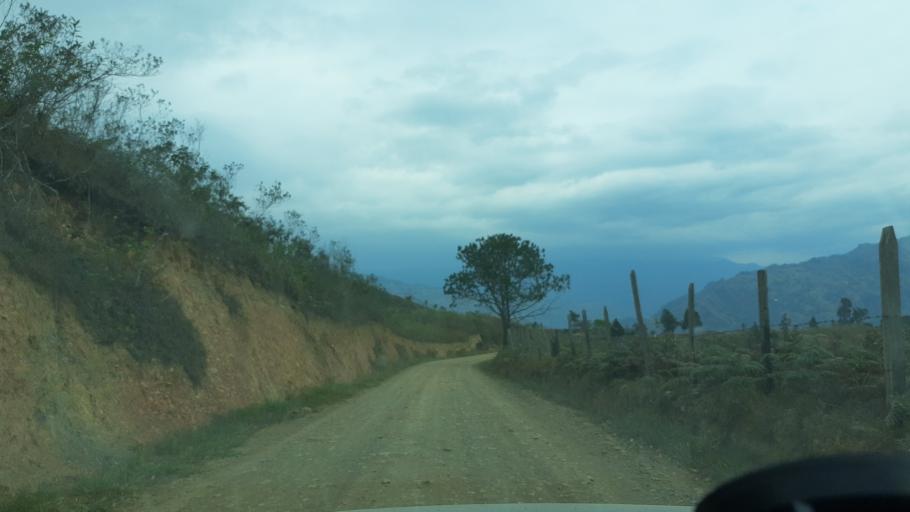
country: CO
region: Boyaca
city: Somondoco
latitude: 4.9869
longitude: -73.3746
